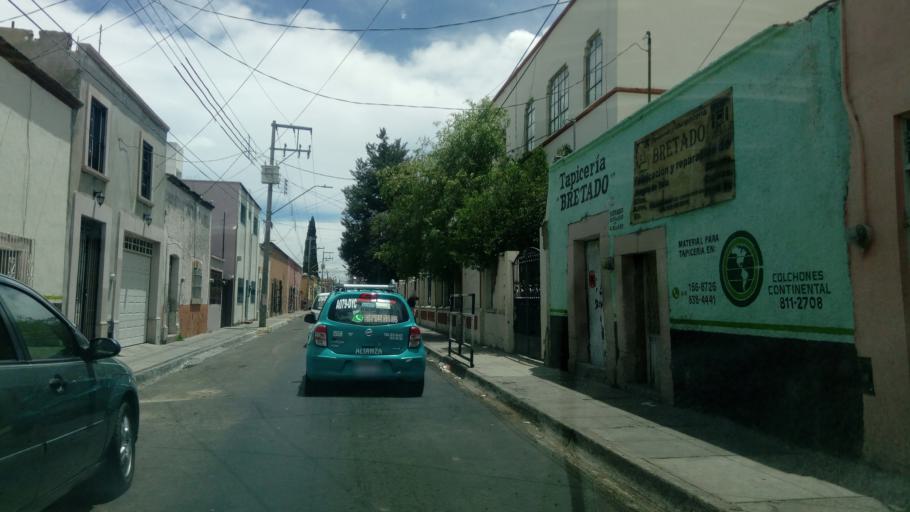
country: MX
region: Durango
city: Victoria de Durango
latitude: 24.0179
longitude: -104.6688
